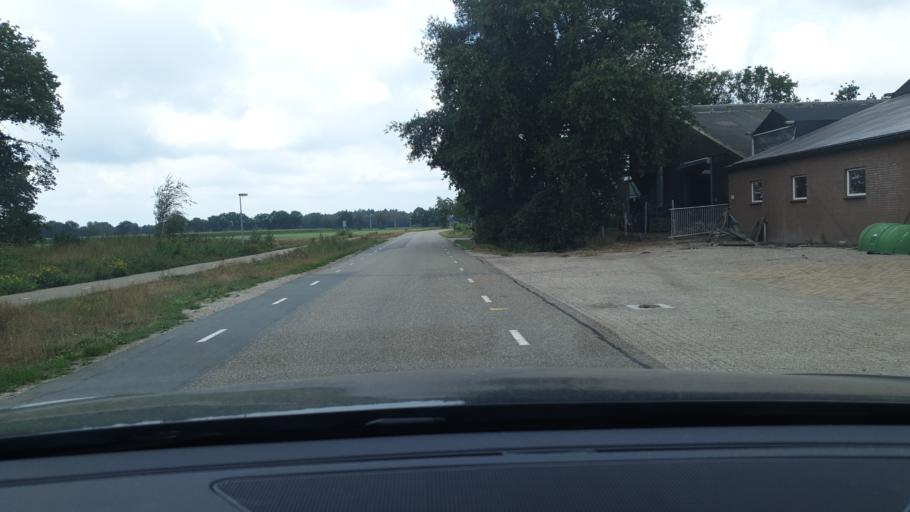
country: NL
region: North Brabant
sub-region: Gemeente Oirschot
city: Oostelbeers
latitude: 51.4515
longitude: 5.2905
